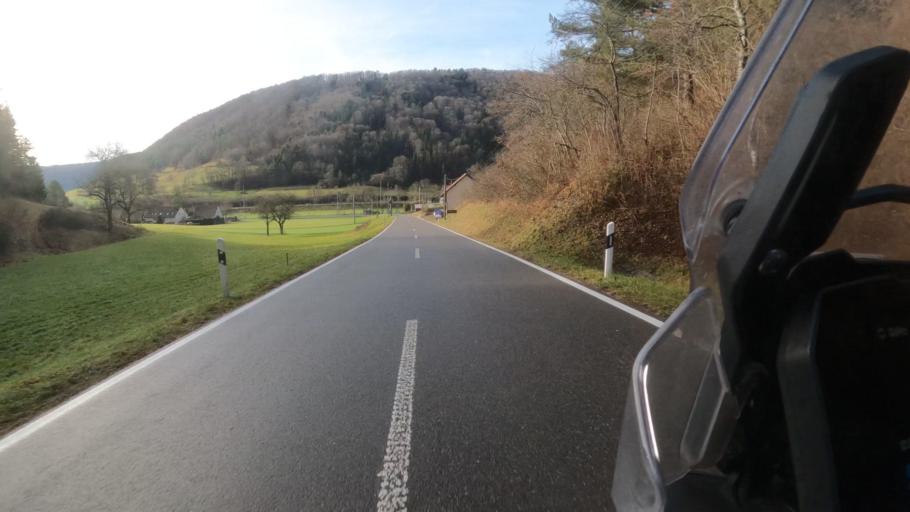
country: DE
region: Baden-Wuerttemberg
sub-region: Freiburg Region
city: Tengen
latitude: 47.7828
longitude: 8.6214
